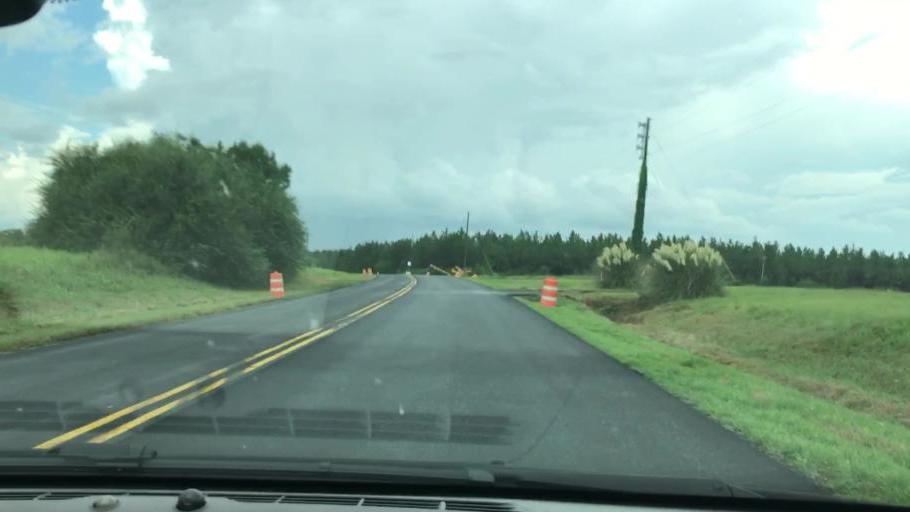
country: US
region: Georgia
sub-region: Early County
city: Blakely
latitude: 31.4091
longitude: -84.9616
